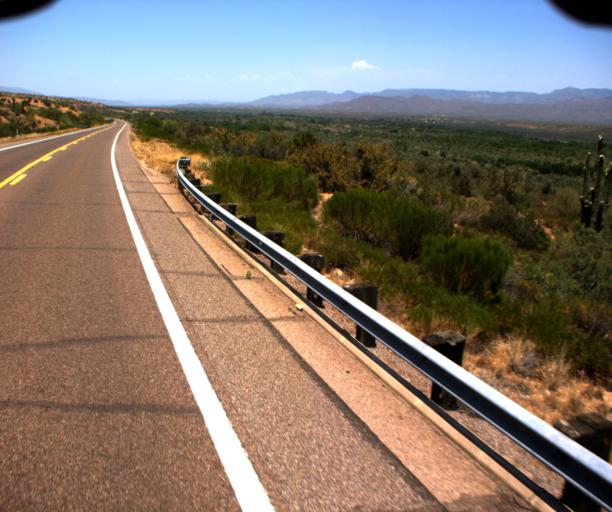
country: US
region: Arizona
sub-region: Gila County
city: Tonto Basin
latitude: 33.7678
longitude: -111.2590
